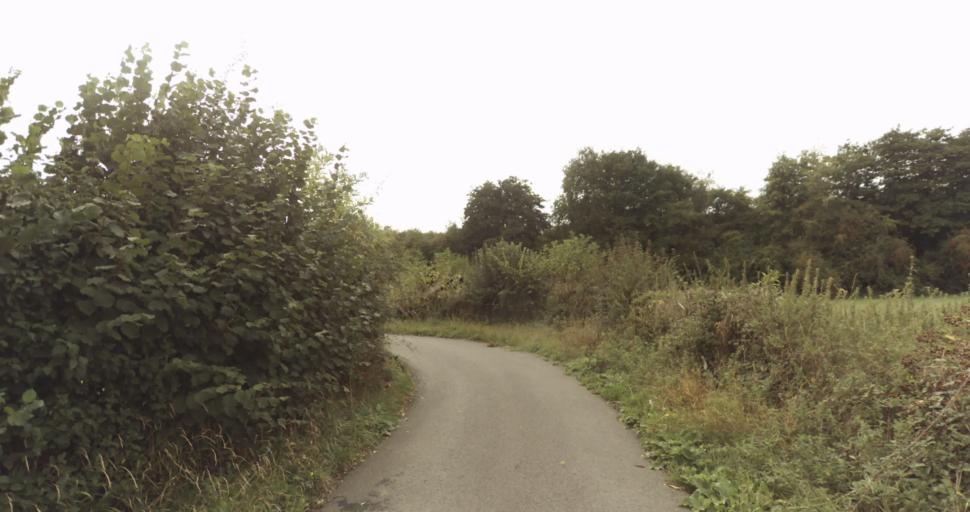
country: FR
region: Lower Normandy
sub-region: Departement de l'Orne
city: Gace
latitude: 48.8136
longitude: 0.2870
